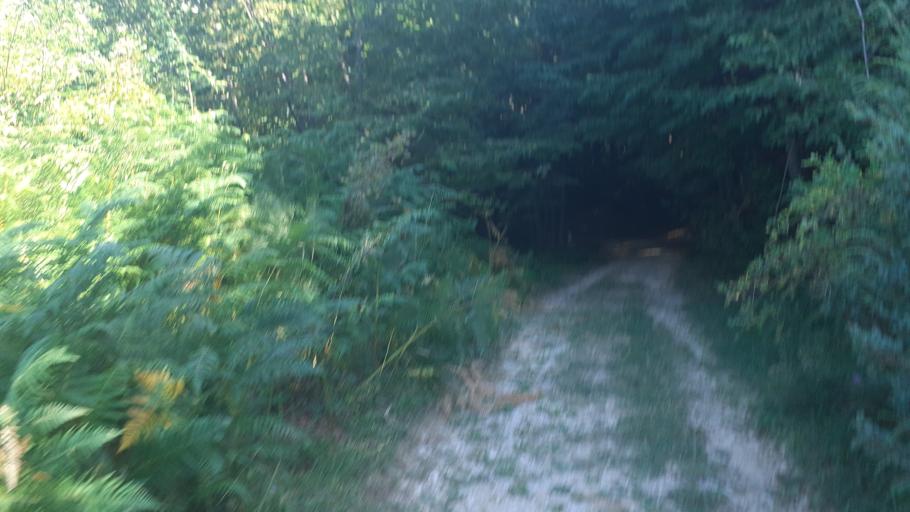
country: IT
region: Abruzzo
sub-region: Provincia di Pescara
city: Sant'Eufemia a Maiella
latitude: 42.1053
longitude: 14.0050
